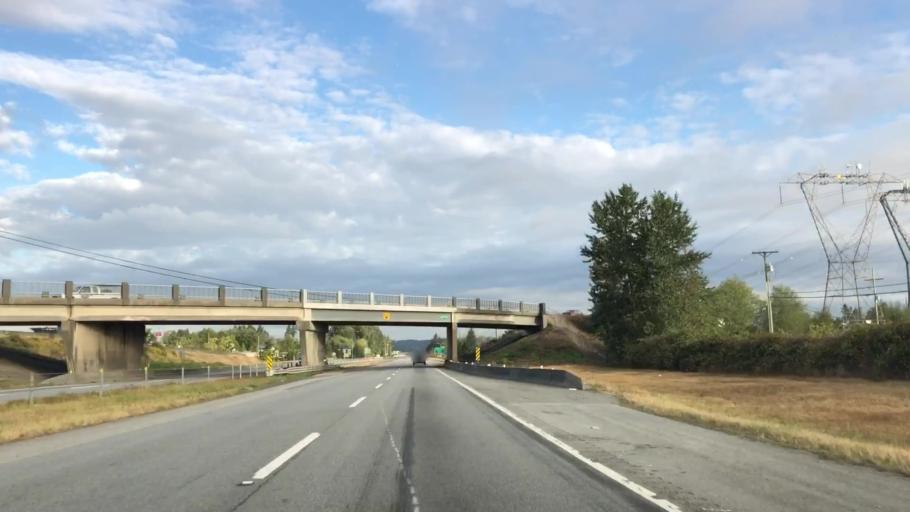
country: CA
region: British Columbia
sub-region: Greater Vancouver Regional District
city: White Rock
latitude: 49.0581
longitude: -122.8004
